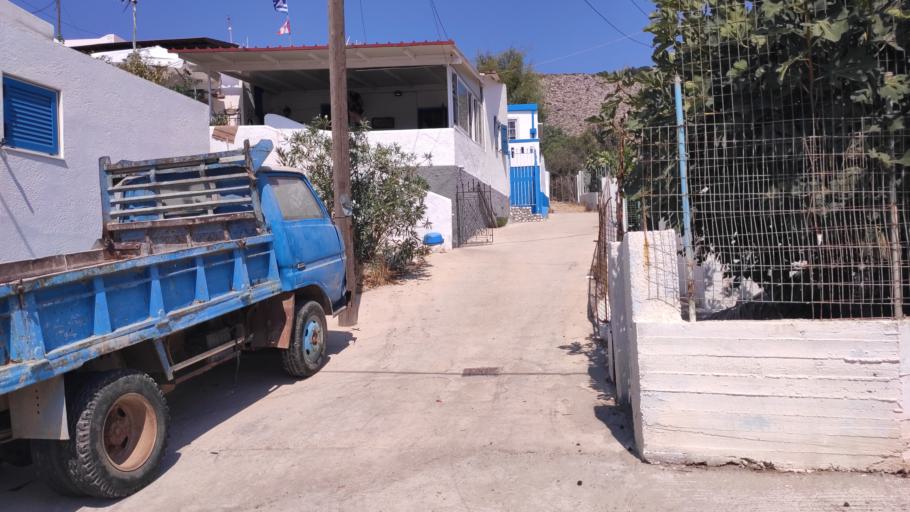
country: GR
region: South Aegean
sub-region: Nomos Dodekanisou
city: Pylion
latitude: 36.9335
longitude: 27.1324
